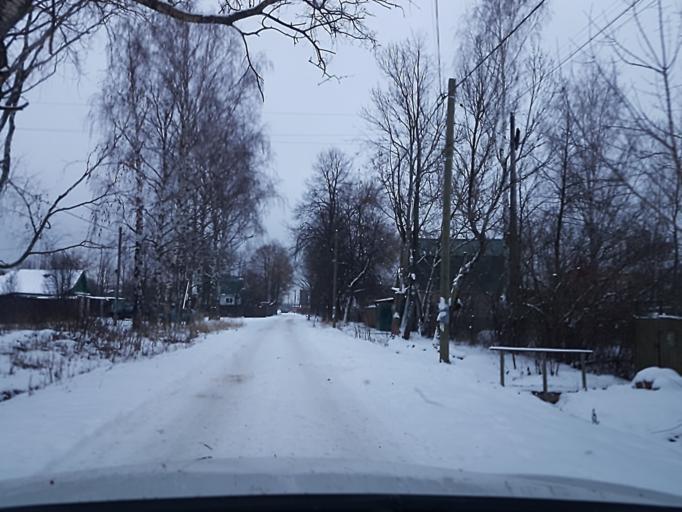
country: RU
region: Tverskaya
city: Novozavidovskiy
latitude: 56.5556
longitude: 36.4243
